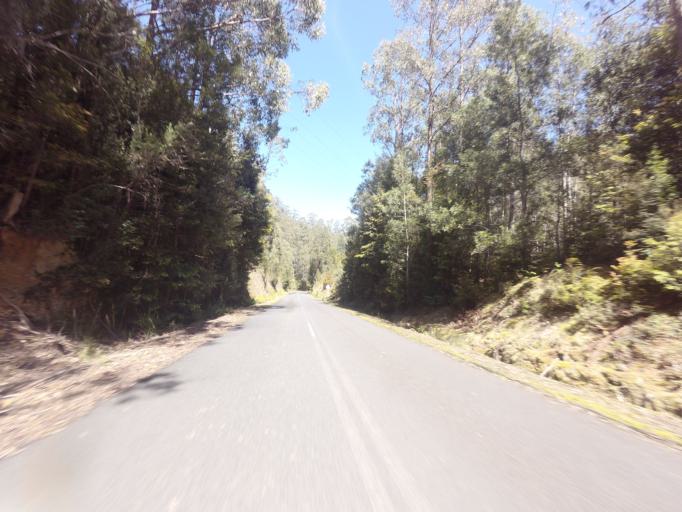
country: AU
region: Tasmania
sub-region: Huon Valley
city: Geeveston
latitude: -42.8176
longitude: 146.3449
